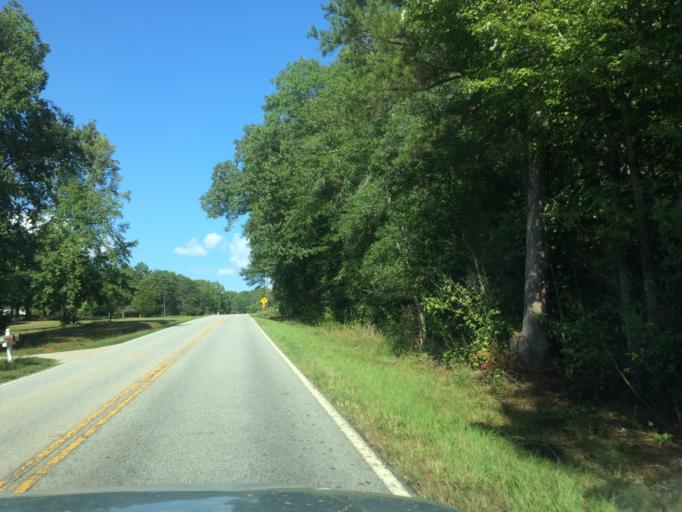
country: US
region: South Carolina
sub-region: Greenwood County
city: Ware Shoals
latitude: 34.4321
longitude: -82.2170
